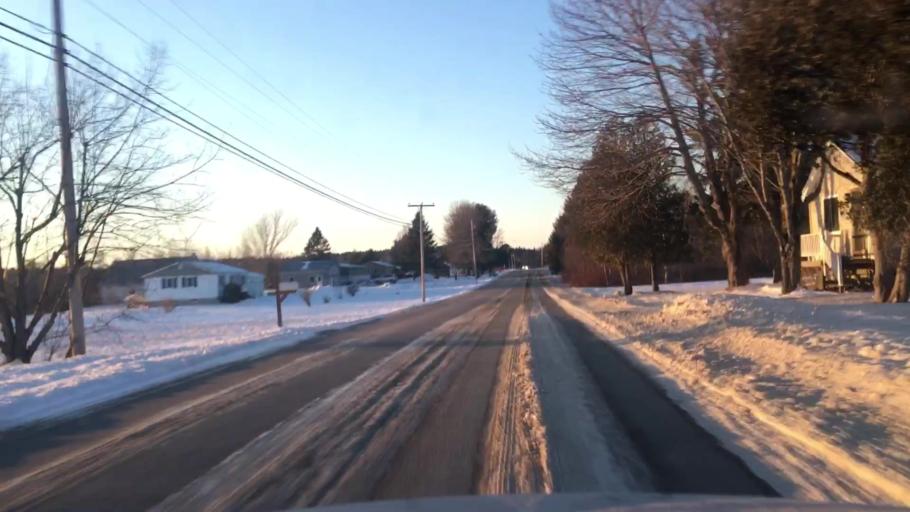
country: US
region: Maine
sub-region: Penobscot County
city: Brewer
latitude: 44.7313
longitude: -68.7592
